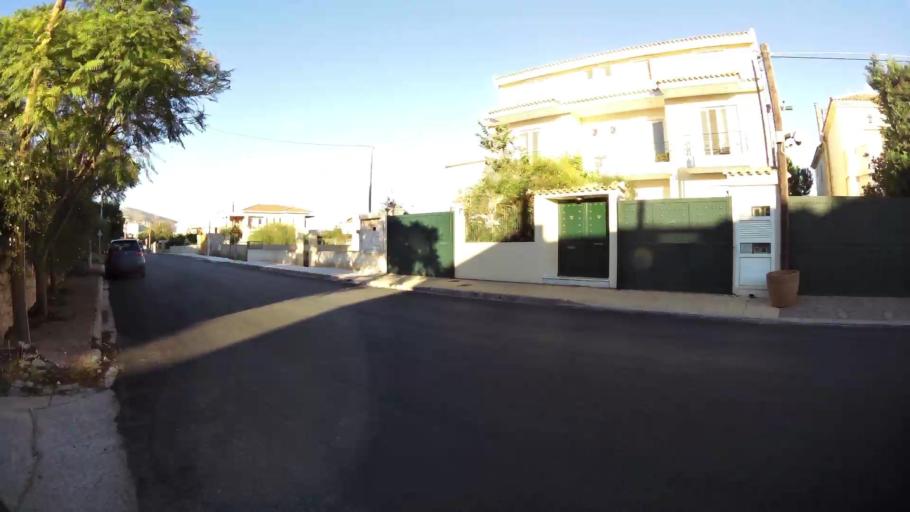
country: GR
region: Attica
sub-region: Nomarchia Anatolikis Attikis
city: Vari
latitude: 37.8263
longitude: 23.8007
